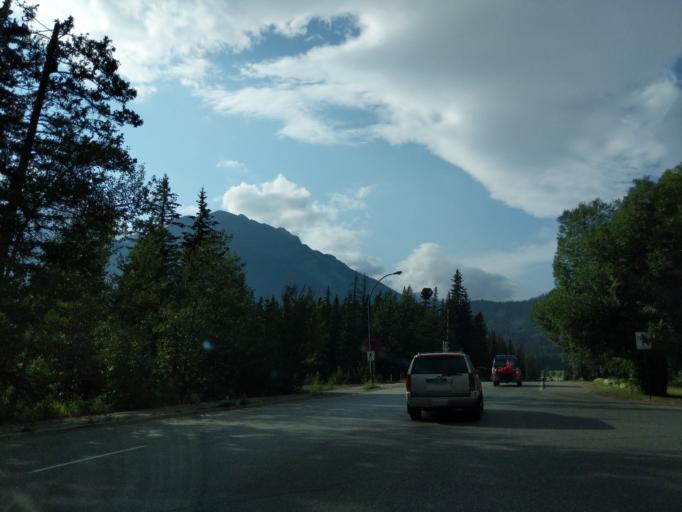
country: CA
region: Alberta
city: Banff
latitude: 51.1804
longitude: -115.5784
